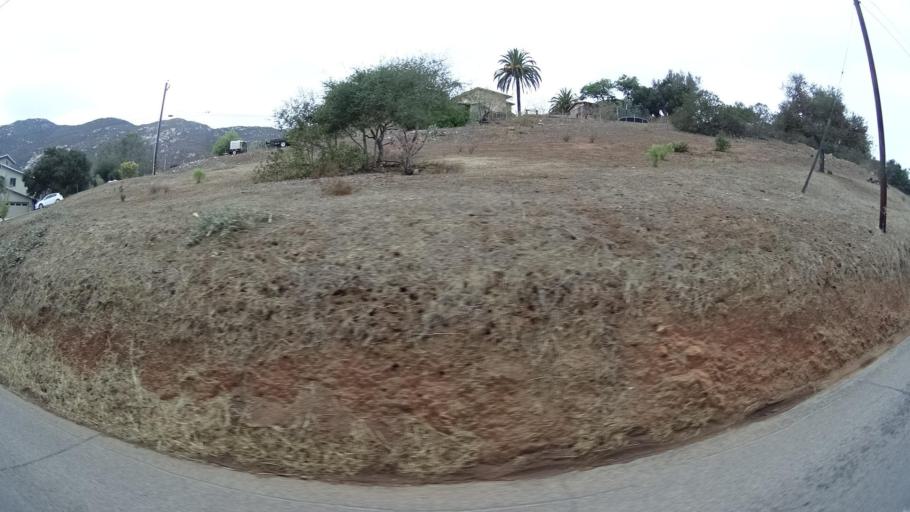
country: US
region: California
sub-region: San Diego County
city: Escondido
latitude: 33.0788
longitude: -117.1156
